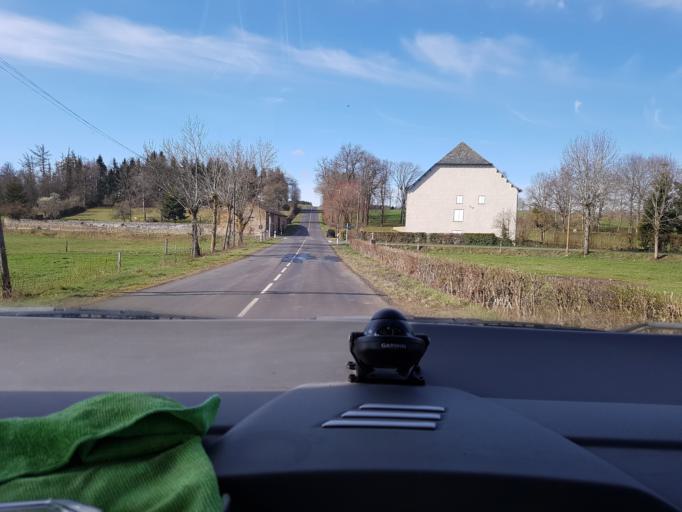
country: FR
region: Auvergne
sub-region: Departement du Cantal
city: Massiac
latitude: 45.1809
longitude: 3.1677
